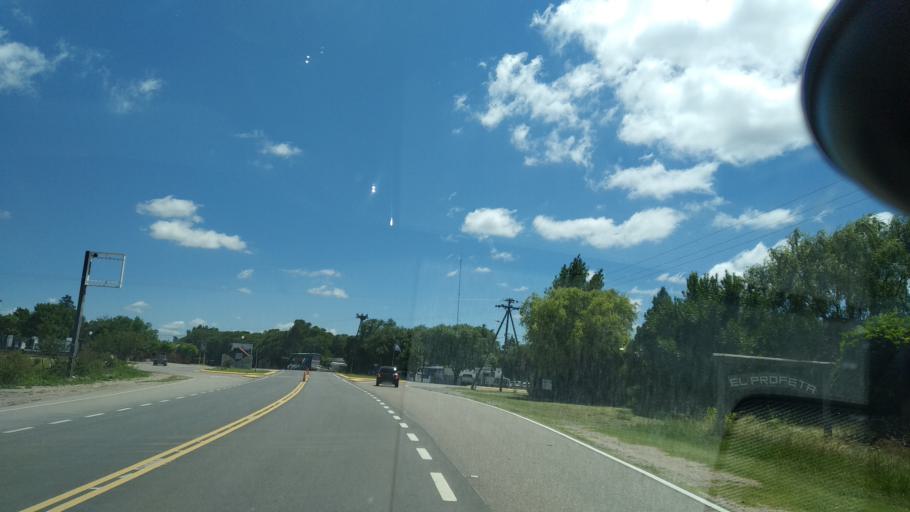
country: AR
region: Cordoba
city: Salsacate
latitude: -31.3470
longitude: -65.0800
